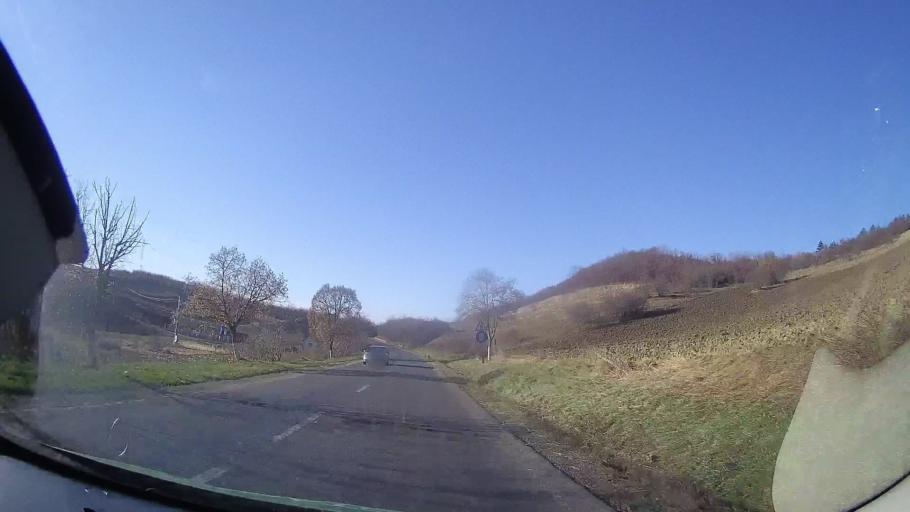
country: RO
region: Mures
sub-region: Comuna Sarmasu
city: Sarmasu
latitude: 46.7908
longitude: 24.1882
